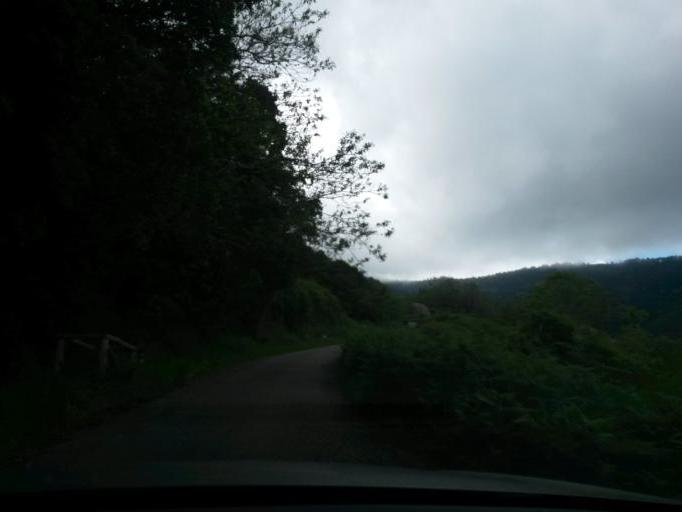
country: IT
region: Tuscany
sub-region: Provincia di Livorno
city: Campo nell'Elba
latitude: 42.7632
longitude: 10.1986
